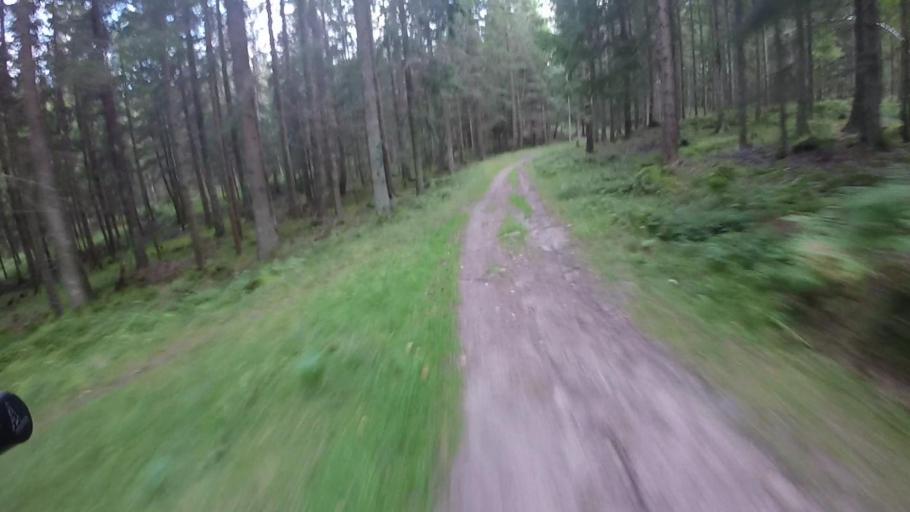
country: SE
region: Vaestra Goetaland
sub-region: Trollhattan
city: Trollhattan
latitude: 58.2558
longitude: 12.2392
